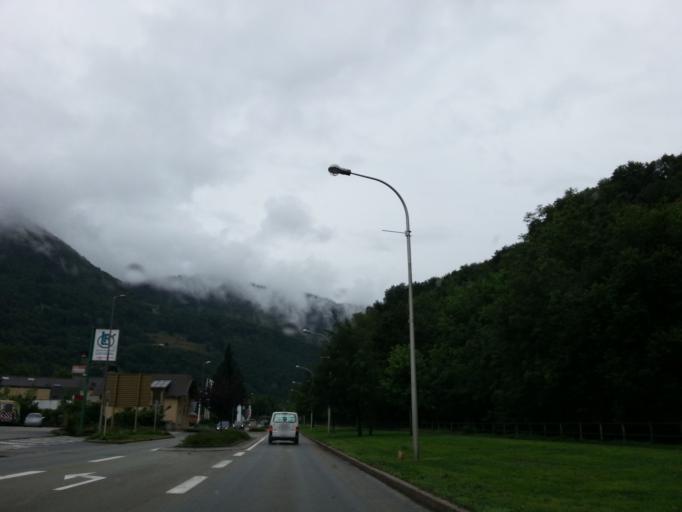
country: FR
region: Rhone-Alpes
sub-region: Departement de la Savoie
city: Ugine
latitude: 45.7441
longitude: 6.4212
